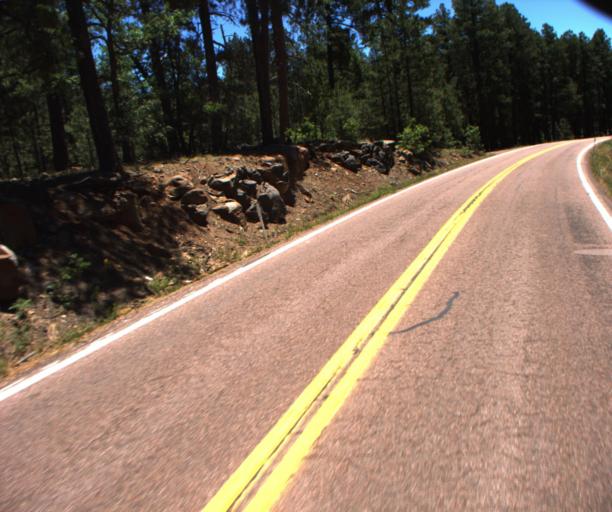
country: US
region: Arizona
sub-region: Gila County
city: Pine
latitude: 34.5136
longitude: -111.3410
